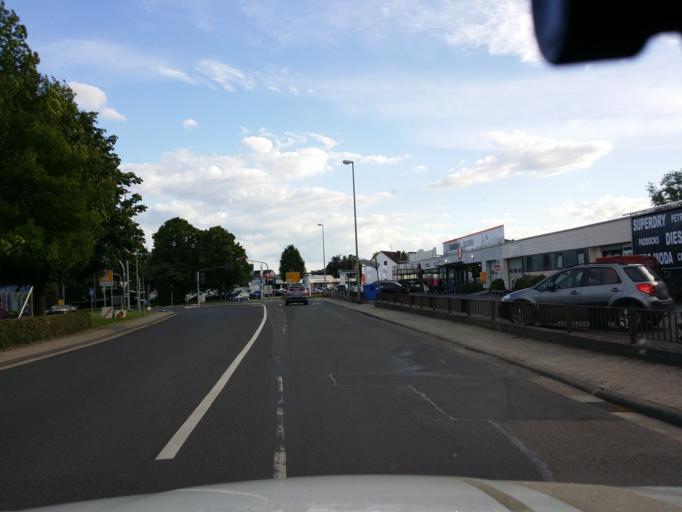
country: DE
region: Hesse
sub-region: Regierungsbezirk Darmstadt
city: Hofheim am Taunus
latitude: 50.0939
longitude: 8.4563
